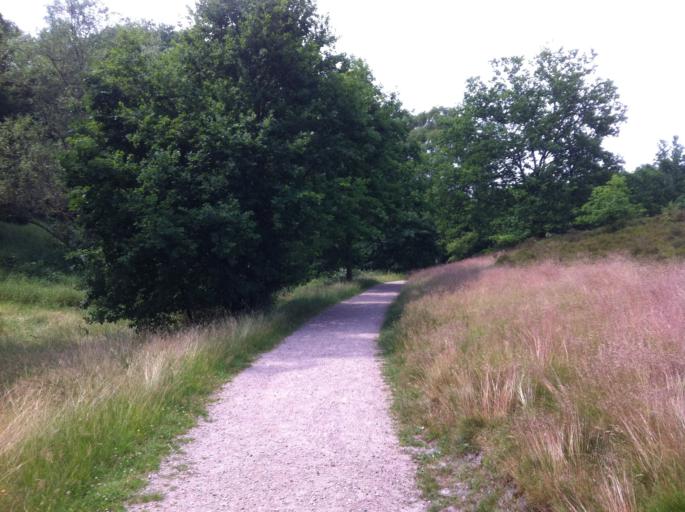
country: DE
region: Lower Saxony
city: Neu Wulmstorf
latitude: 53.4655
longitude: 9.8699
